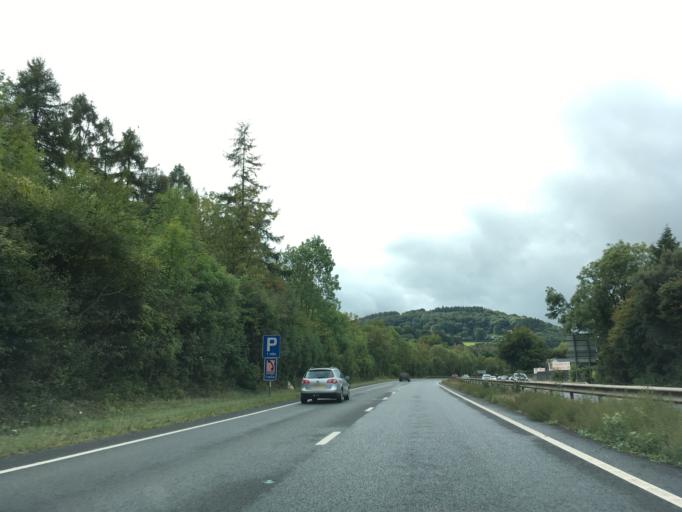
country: GB
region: England
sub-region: Herefordshire
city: Whitchurch
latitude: 51.8535
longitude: -2.6558
